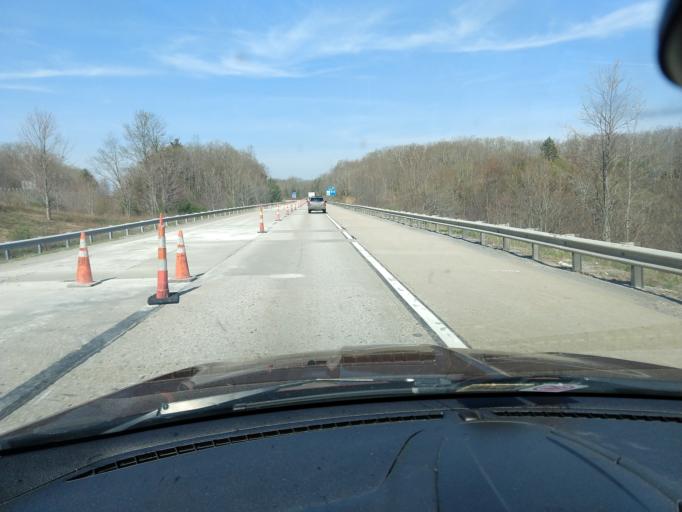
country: US
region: West Virginia
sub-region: Raleigh County
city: Daniels
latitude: 37.7749
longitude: -81.0911
